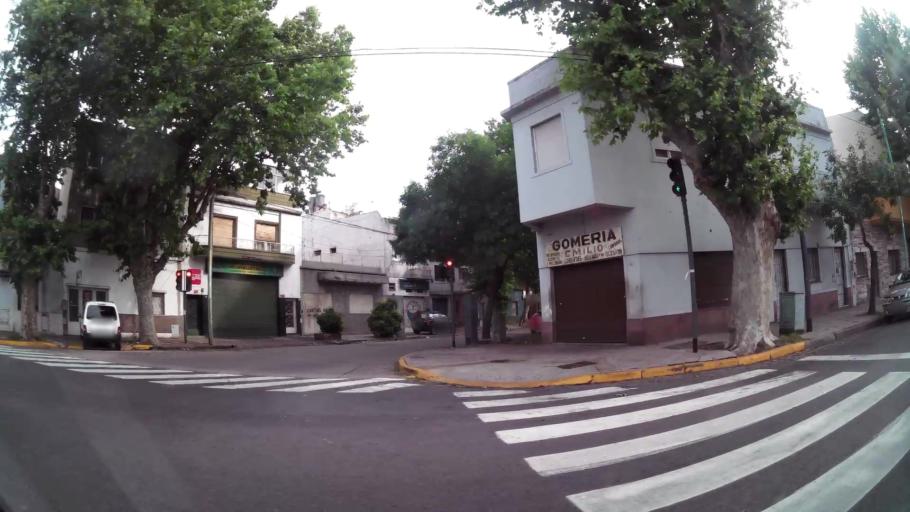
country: AR
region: Buenos Aires F.D.
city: Villa Lugano
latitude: -34.6451
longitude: -58.4306
